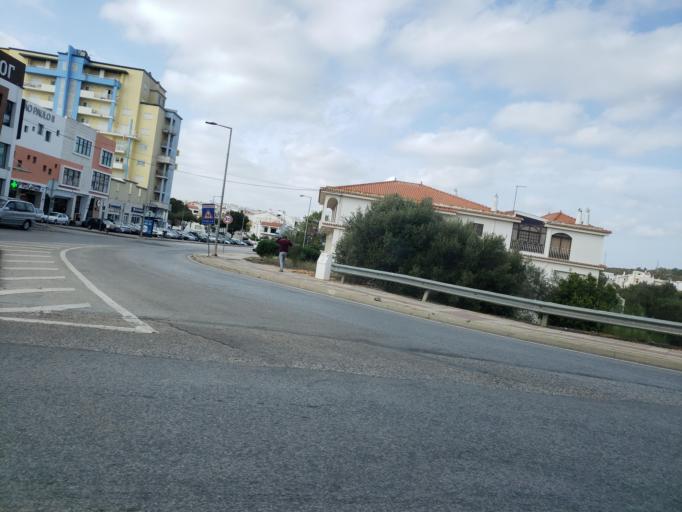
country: PT
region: Faro
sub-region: Portimao
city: Portimao
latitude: 37.1439
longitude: -8.5489
